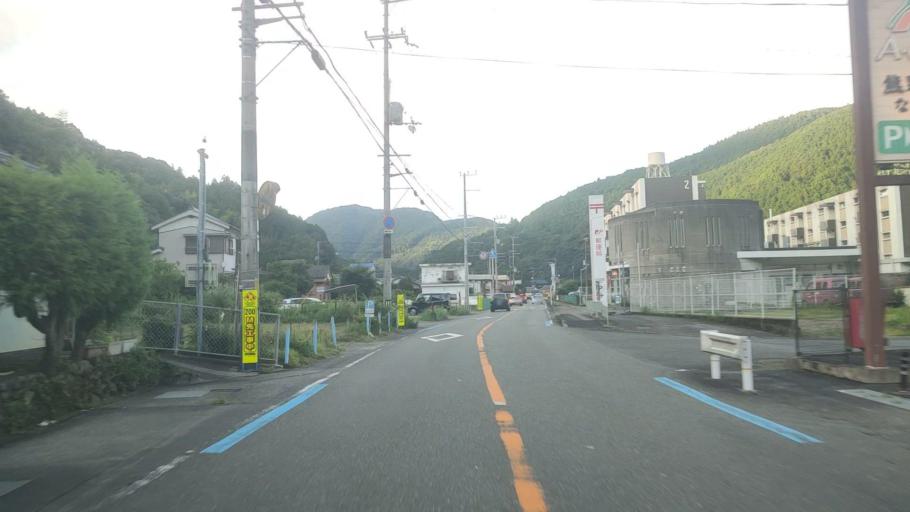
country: JP
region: Wakayama
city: Tanabe
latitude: 33.7921
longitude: 135.5168
